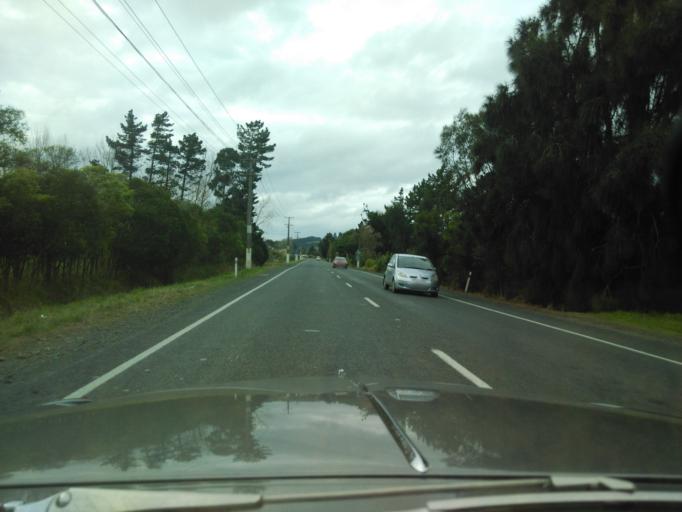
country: NZ
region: Auckland
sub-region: Auckland
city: Parakai
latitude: -36.6823
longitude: 174.4350
